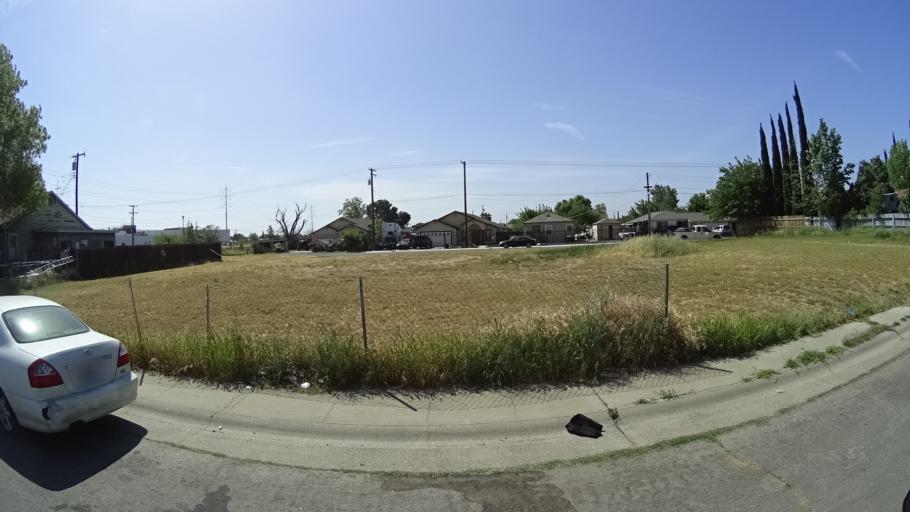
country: US
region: California
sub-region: Sacramento County
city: Parkway
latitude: 38.5035
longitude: -121.4747
